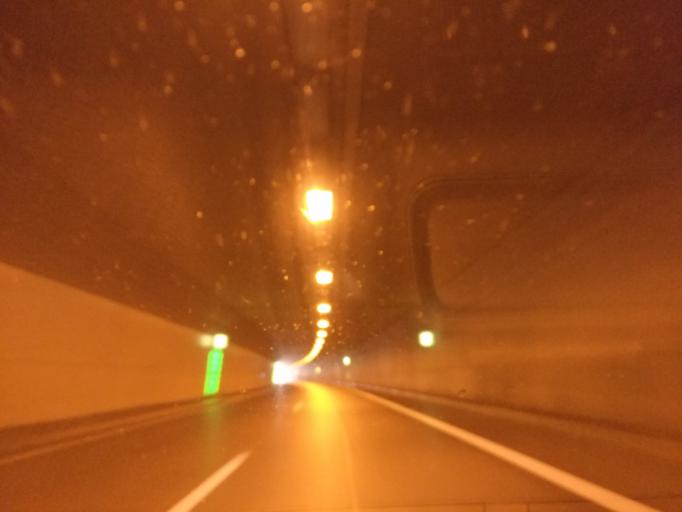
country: DE
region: Baden-Wuerttemberg
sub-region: Regierungsbezirk Stuttgart
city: Schorndorf
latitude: 48.8224
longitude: 9.5327
